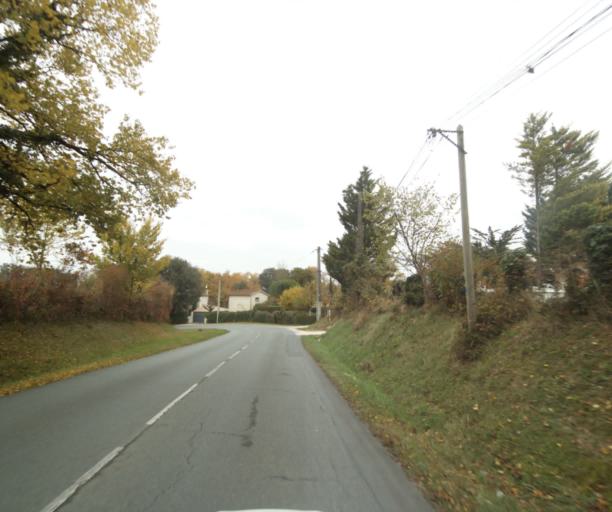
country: FR
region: Poitou-Charentes
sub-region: Departement de la Charente-Maritime
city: Les Gonds
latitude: 45.7236
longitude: -0.6345
